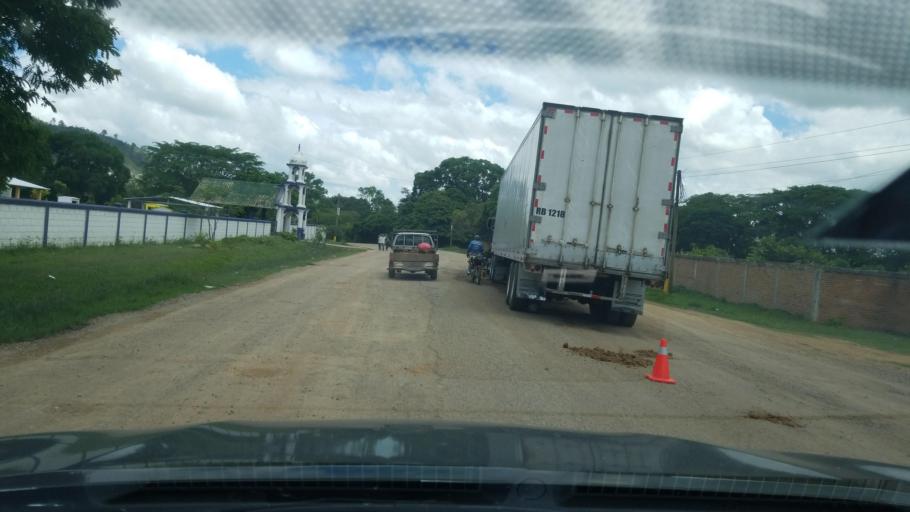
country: HN
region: Francisco Morazan
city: Talanga
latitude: 14.3958
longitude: -87.0784
